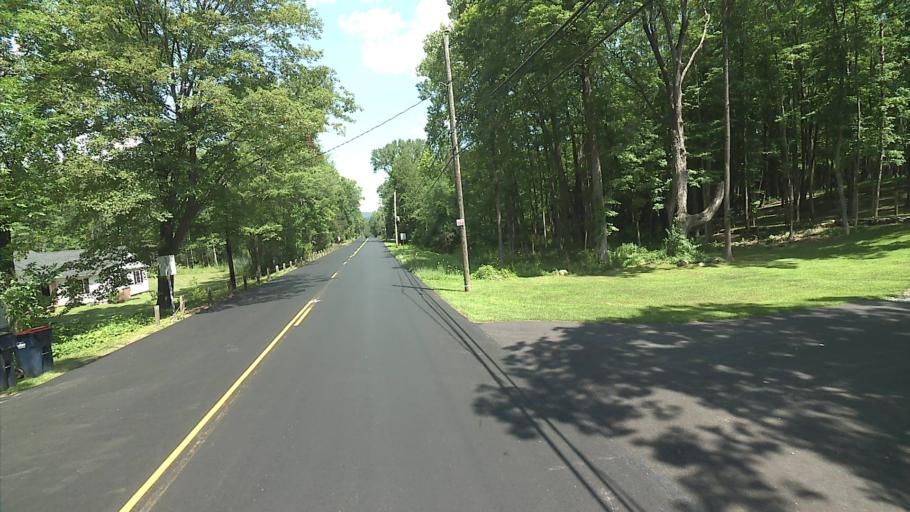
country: US
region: Connecticut
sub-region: Litchfield County
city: Canaan
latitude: 41.9879
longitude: -73.3611
